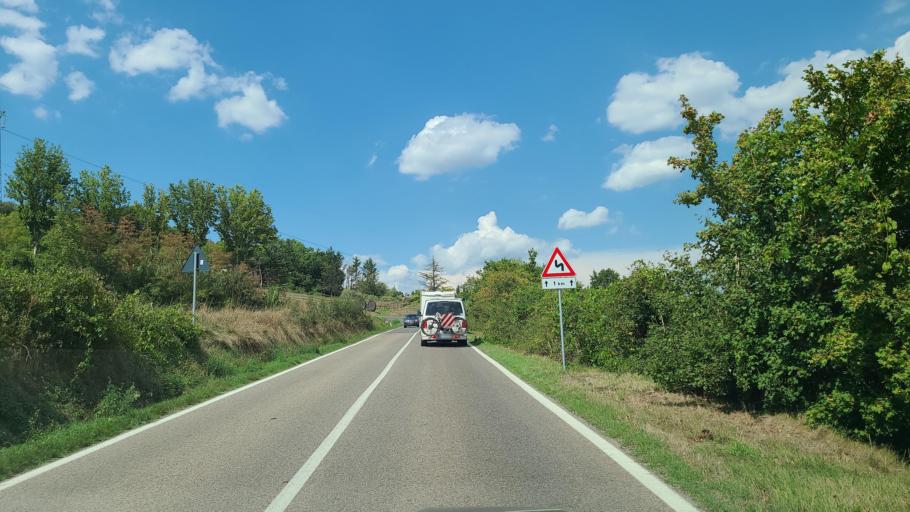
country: IT
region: Tuscany
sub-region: Provincia di Siena
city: Colle di Val d'Elsa
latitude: 43.4120
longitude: 11.0644
